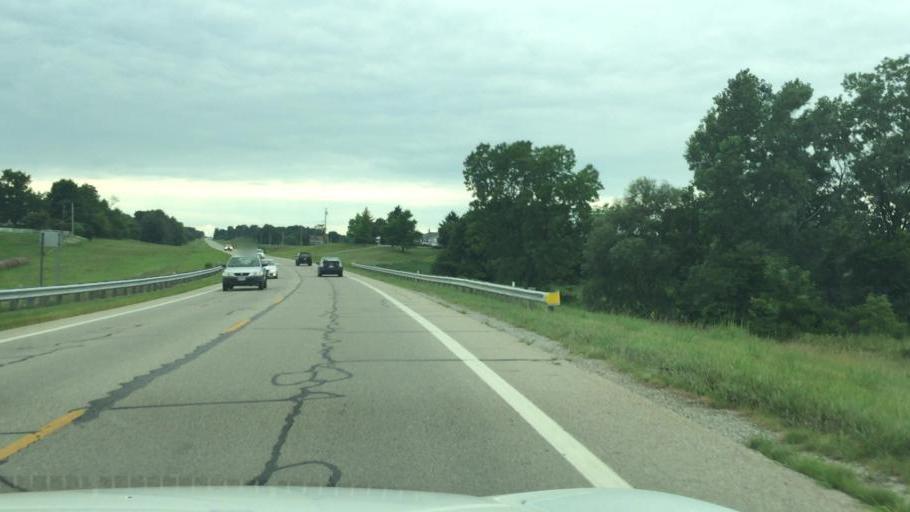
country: US
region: Ohio
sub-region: Champaign County
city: Mechanicsburg
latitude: 40.0785
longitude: -83.5792
